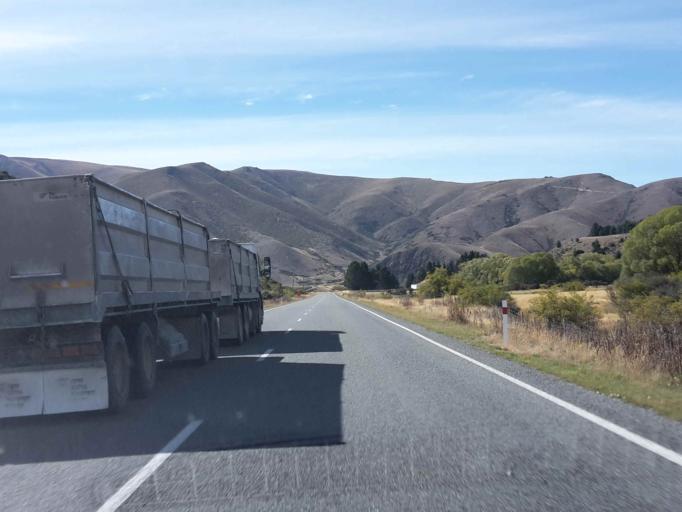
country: NZ
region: Otago
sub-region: Queenstown-Lakes District
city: Wanaka
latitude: -44.5044
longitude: 169.7460
